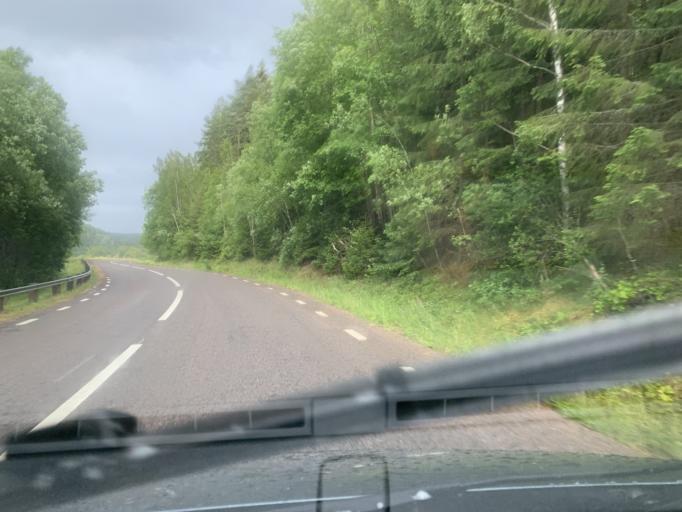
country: SE
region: Kalmar
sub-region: Vasterviks Kommun
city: Overum
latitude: 58.0171
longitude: 16.1569
